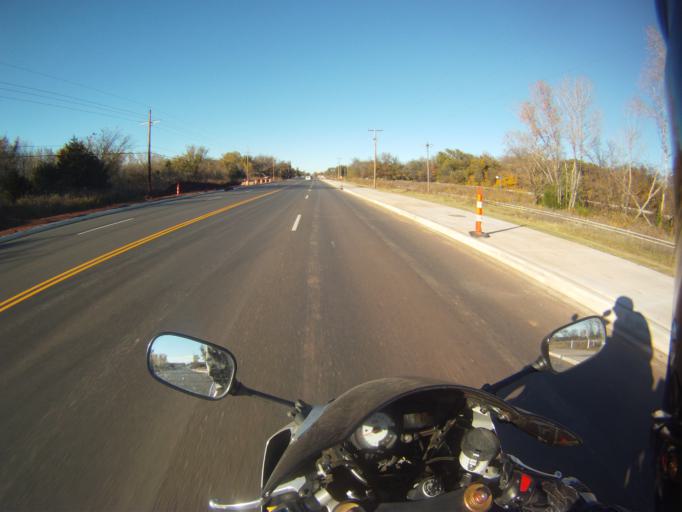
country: US
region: Oklahoma
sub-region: Payne County
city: Stillwater
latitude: 36.1211
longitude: -97.1231
